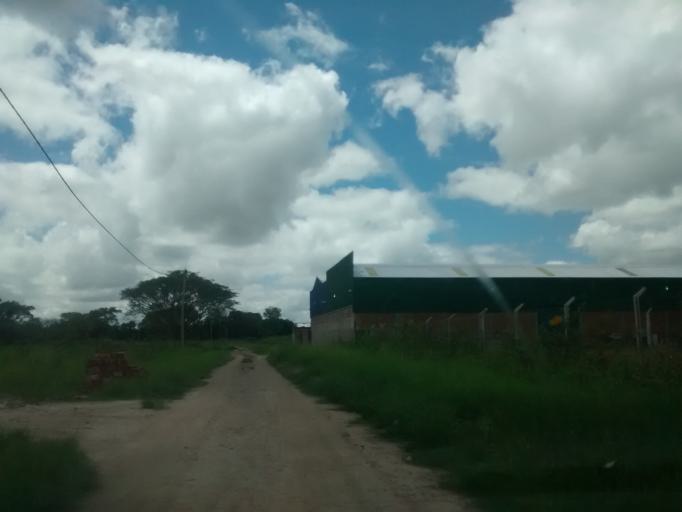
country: AR
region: Chaco
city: Fontana
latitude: -27.4139
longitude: -58.9970
